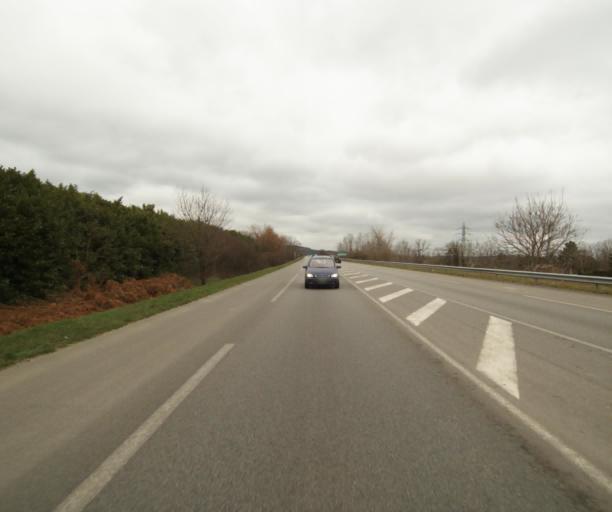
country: FR
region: Midi-Pyrenees
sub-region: Departement de l'Ariege
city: Pamiers
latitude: 43.1365
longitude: 1.6195
